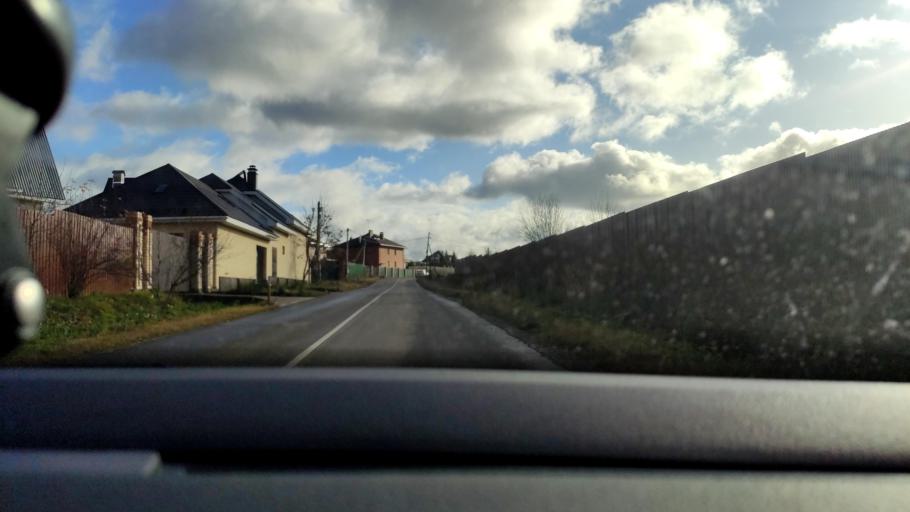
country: RU
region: Moskovskaya
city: Yermolino
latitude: 56.1562
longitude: 37.4802
